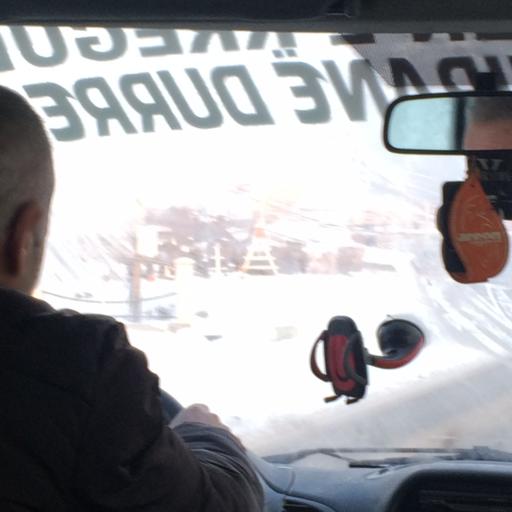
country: XK
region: Pristina
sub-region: Komuna e Drenasit
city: Glogovac
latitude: 42.5858
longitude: 20.8980
